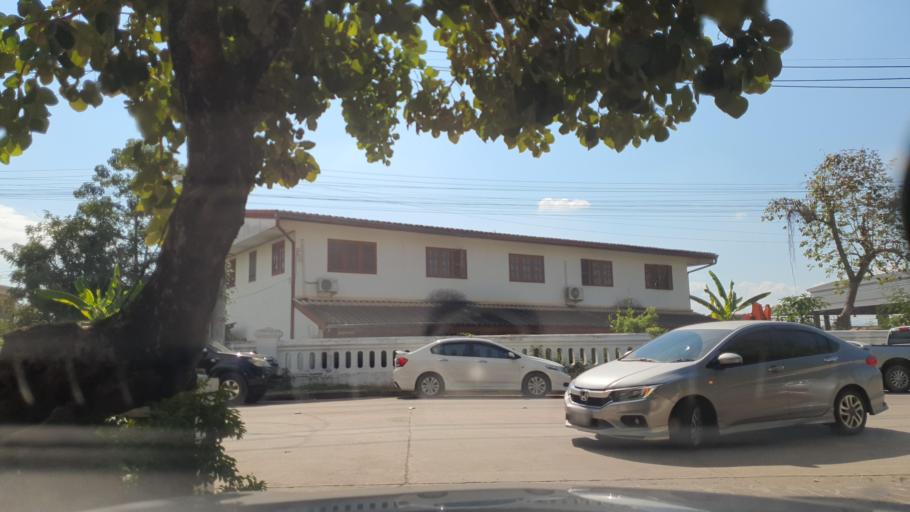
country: TH
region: Nan
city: Nan
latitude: 18.7864
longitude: 100.7749
